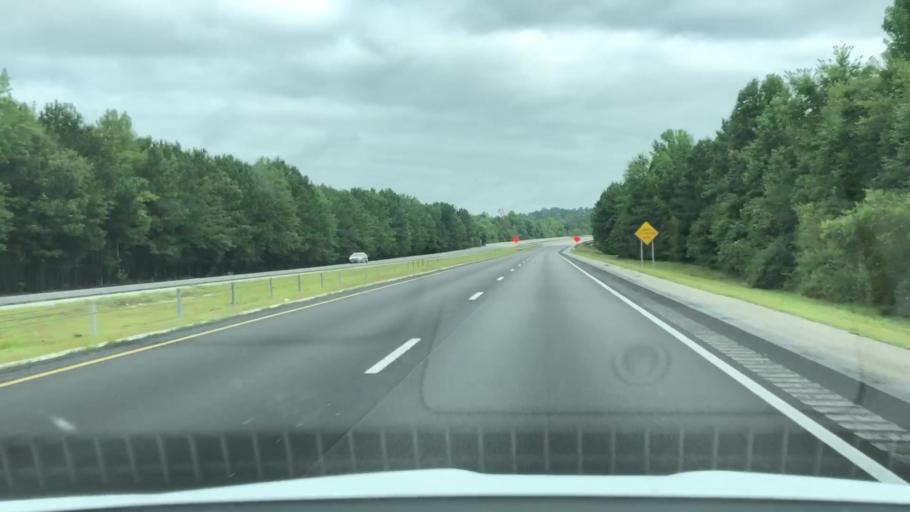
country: US
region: North Carolina
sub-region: Wayne County
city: Fremont
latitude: 35.5785
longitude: -77.9896
